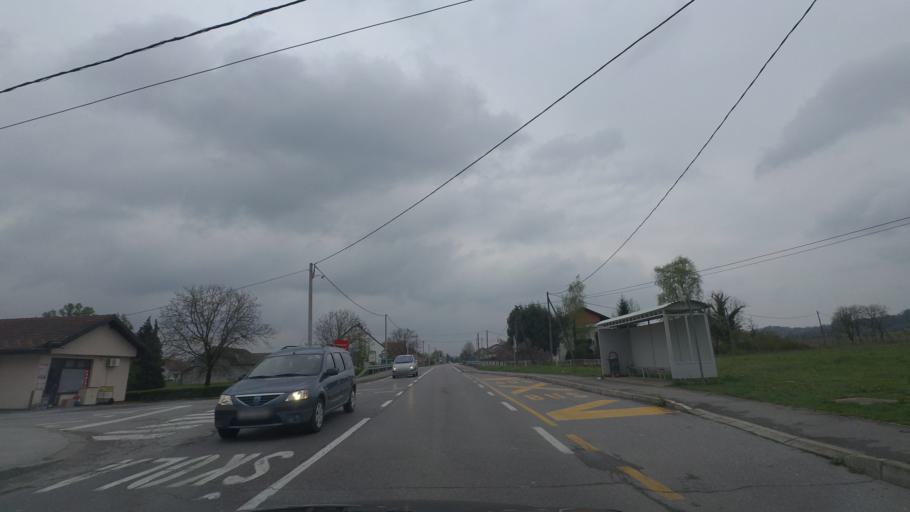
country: HR
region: Zagrebacka
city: Jastrebarsko
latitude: 45.6029
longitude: 15.5983
